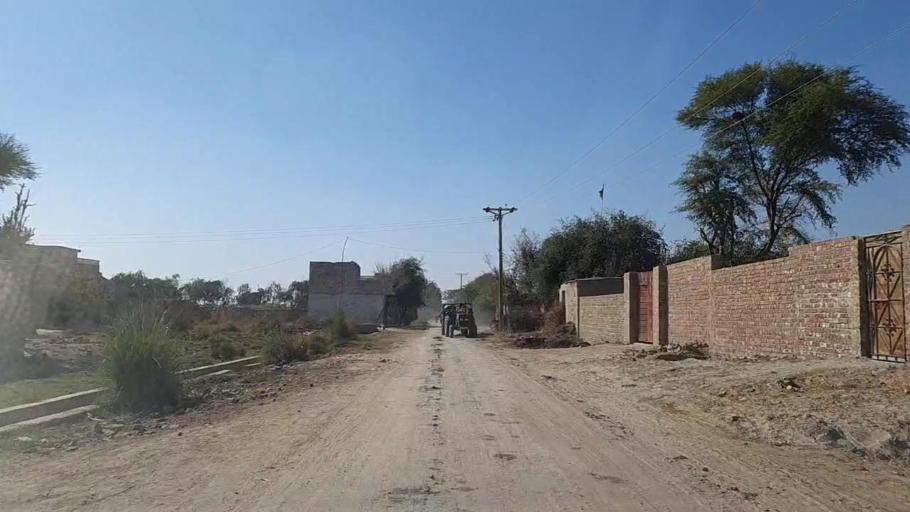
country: PK
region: Sindh
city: Nawabshah
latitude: 26.2445
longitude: 68.4336
